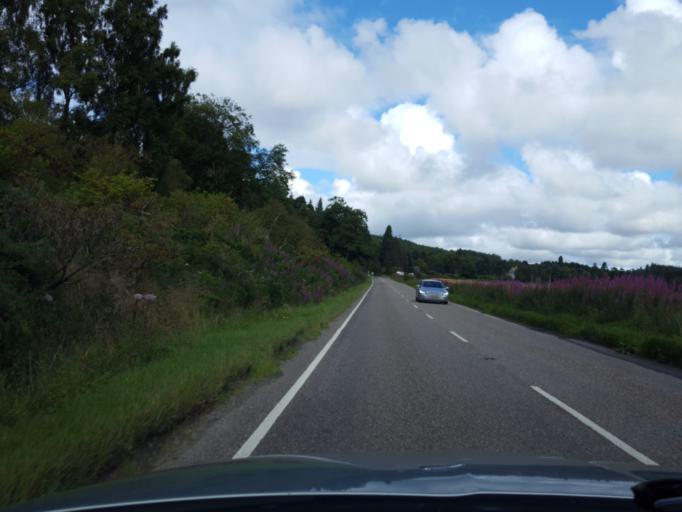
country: GB
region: Scotland
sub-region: Moray
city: Rothes
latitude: 57.5503
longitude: -3.2398
